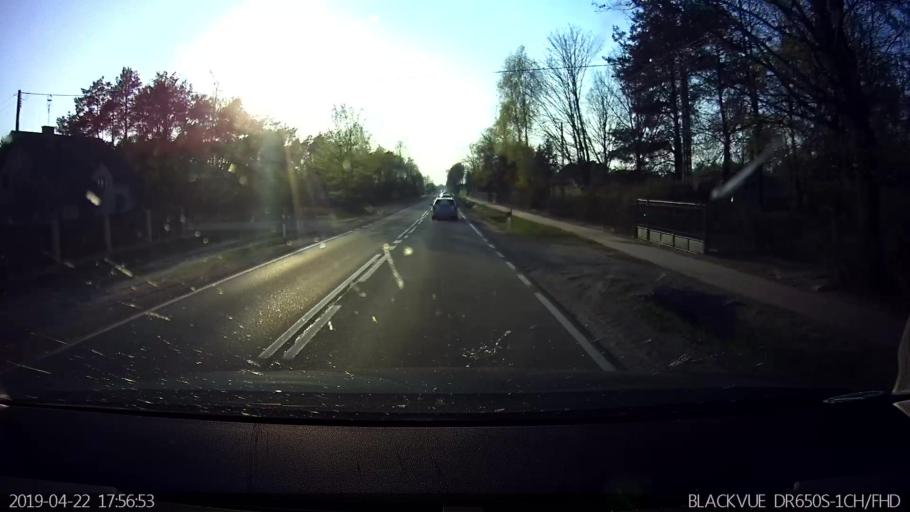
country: PL
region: Masovian Voivodeship
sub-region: Powiat wegrowski
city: Korytnica
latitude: 52.4668
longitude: 21.9005
